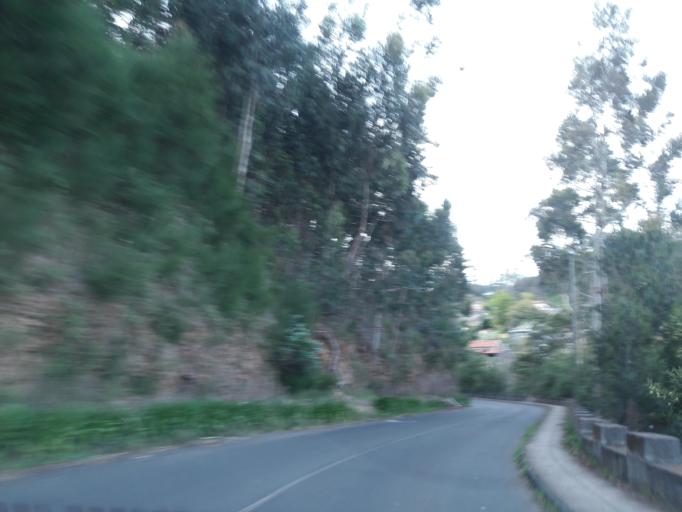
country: PT
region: Madeira
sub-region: Santa Cruz
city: Camacha
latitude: 32.6905
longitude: -16.8662
